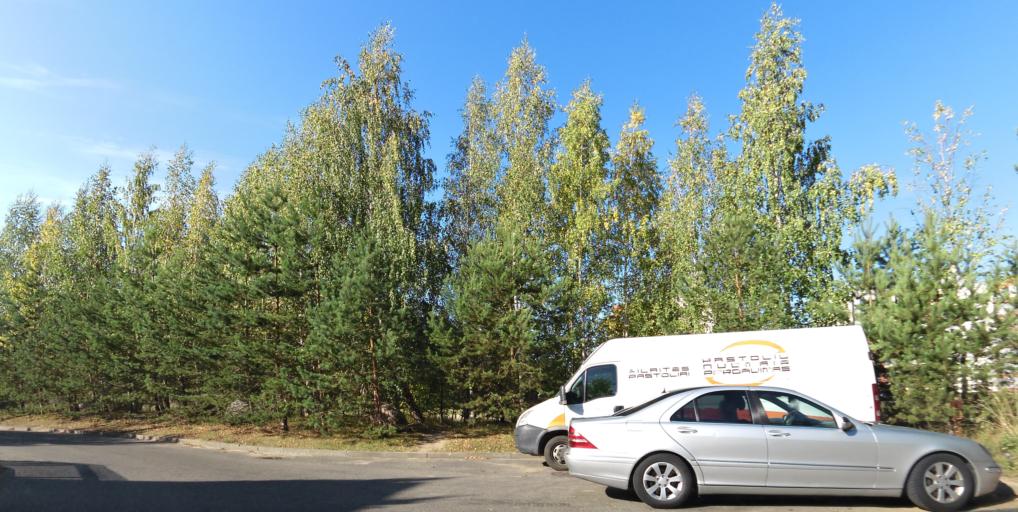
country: LT
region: Vilnius County
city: Pilaite
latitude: 54.7139
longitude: 25.1897
